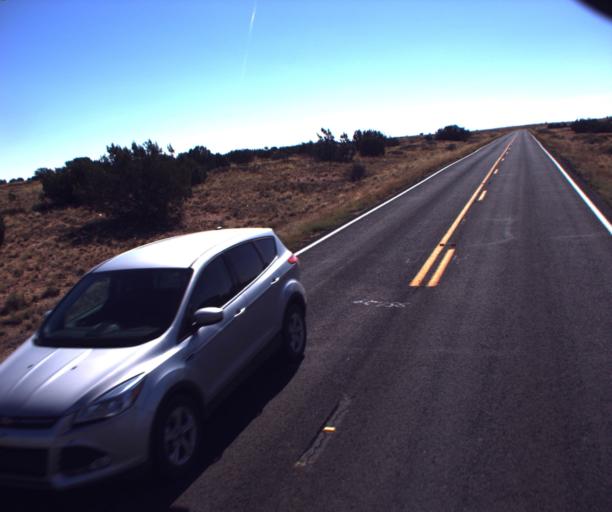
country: US
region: Arizona
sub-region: Coconino County
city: Tuba City
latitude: 35.9220
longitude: -110.8576
